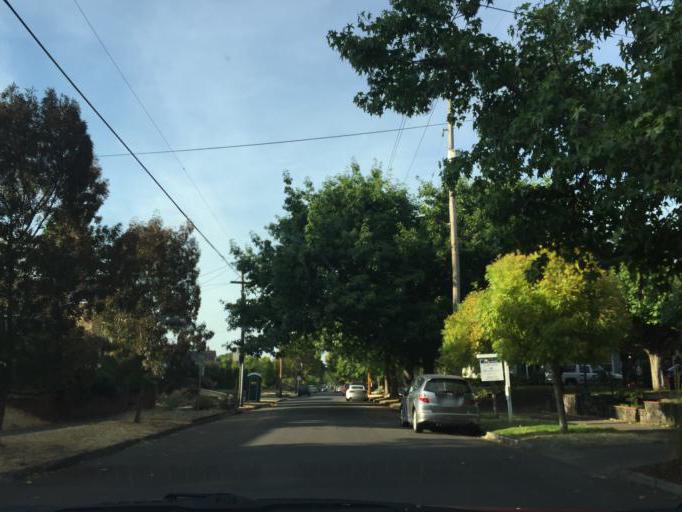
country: US
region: Oregon
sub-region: Multnomah County
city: Portland
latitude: 45.5557
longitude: -122.6297
